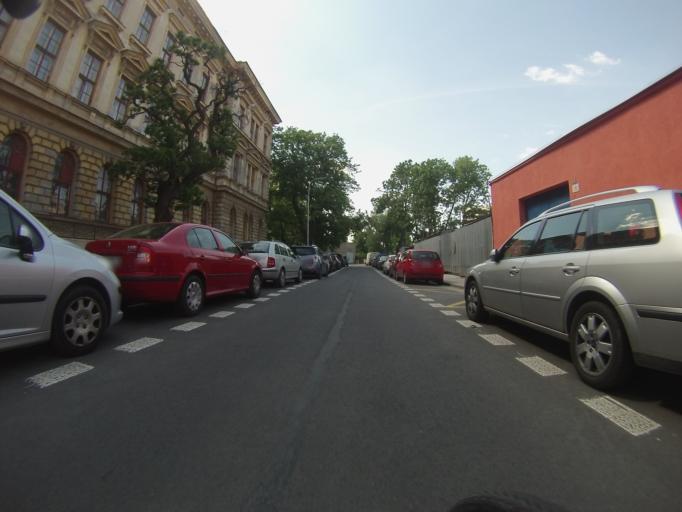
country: CZ
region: South Moravian
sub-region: Mesto Brno
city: Brno
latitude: 49.1893
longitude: 16.6197
